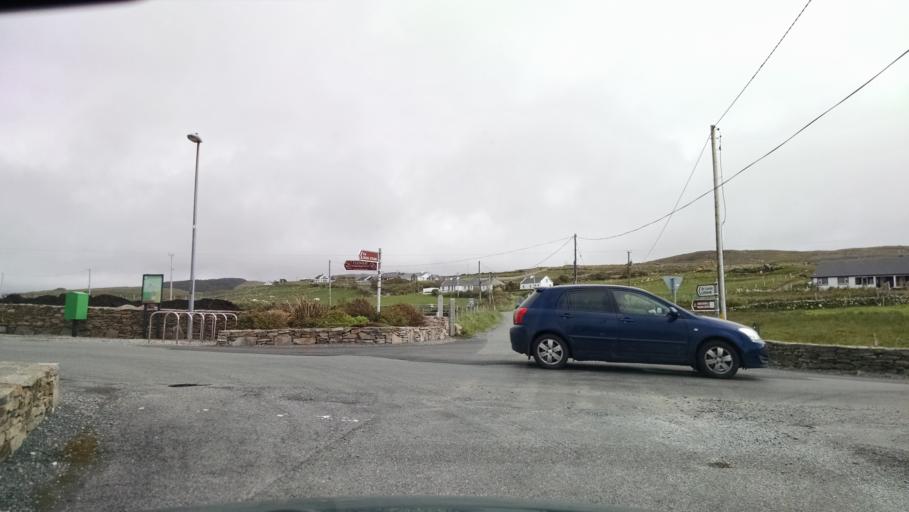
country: IE
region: Connaught
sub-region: County Galway
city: Clifden
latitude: 53.7129
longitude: -9.8843
